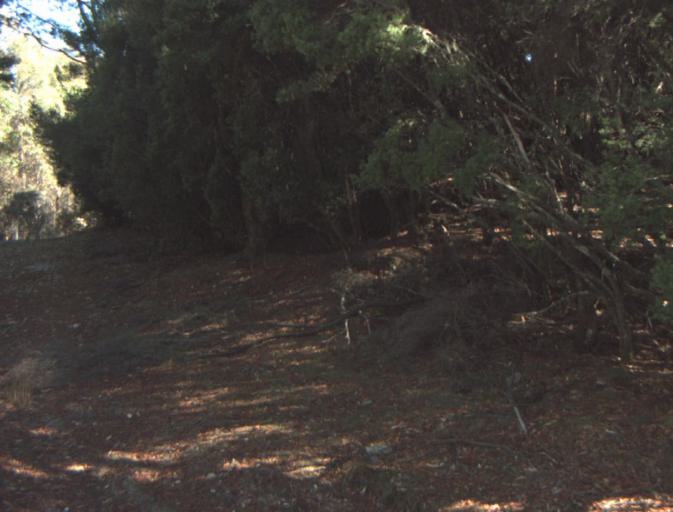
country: AU
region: Tasmania
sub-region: Dorset
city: Scottsdale
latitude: -41.2937
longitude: 147.3542
